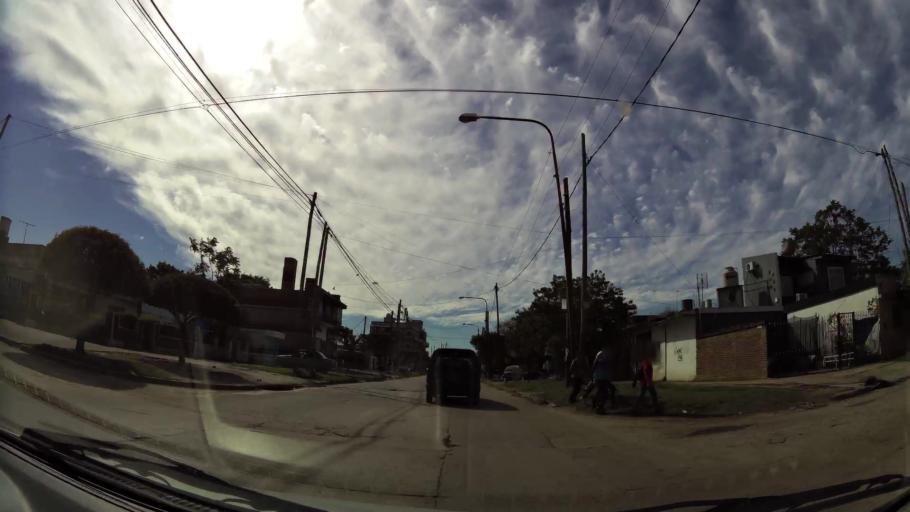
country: AR
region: Buenos Aires
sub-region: Partido de Almirante Brown
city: Adrogue
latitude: -34.7713
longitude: -58.3141
